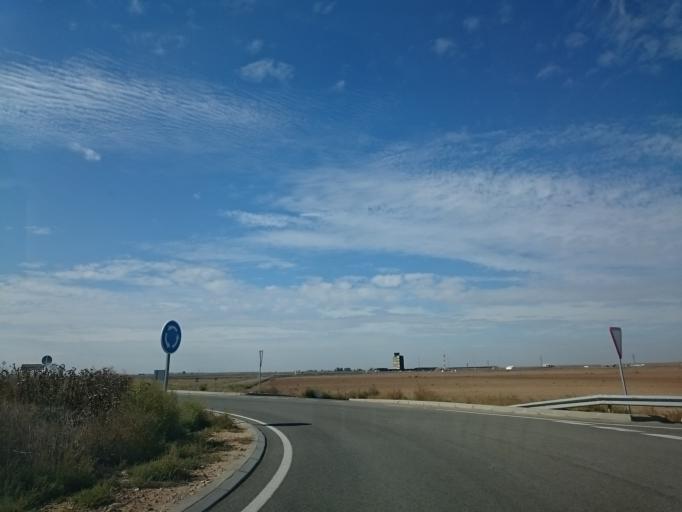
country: ES
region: Catalonia
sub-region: Provincia de Lleida
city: Alguaire
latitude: 41.7315
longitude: 0.5577
